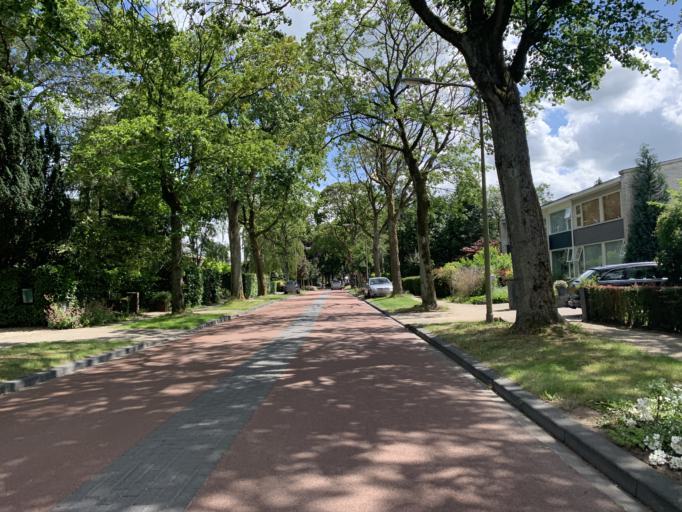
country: NL
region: Groningen
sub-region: Gemeente Haren
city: Haren
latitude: 53.1698
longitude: 6.6126
